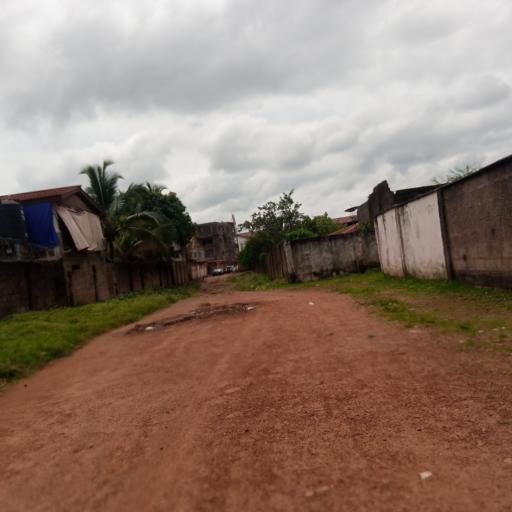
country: SL
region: Eastern Province
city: Kenema
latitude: 7.8832
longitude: -11.1902
